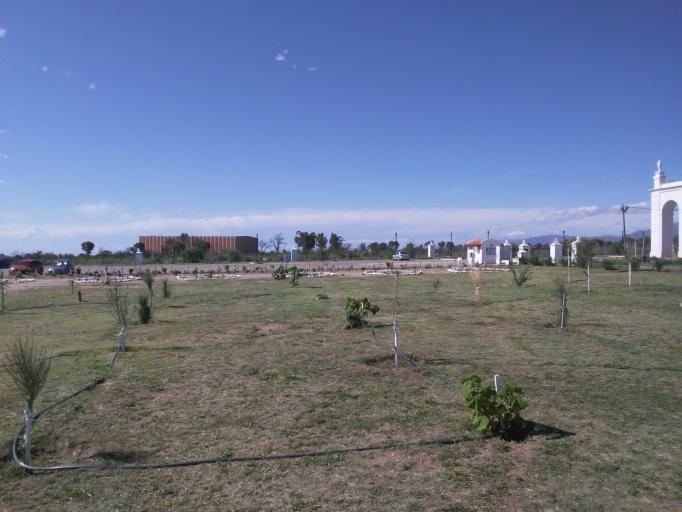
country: AR
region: San Luis
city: La Punta
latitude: -33.1598
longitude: -66.3252
